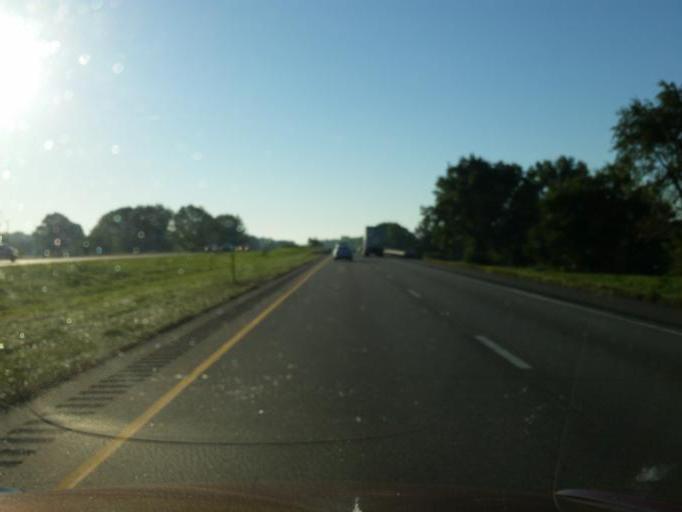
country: US
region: Pennsylvania
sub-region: Lancaster County
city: Salunga
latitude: 40.1138
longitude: -76.4478
